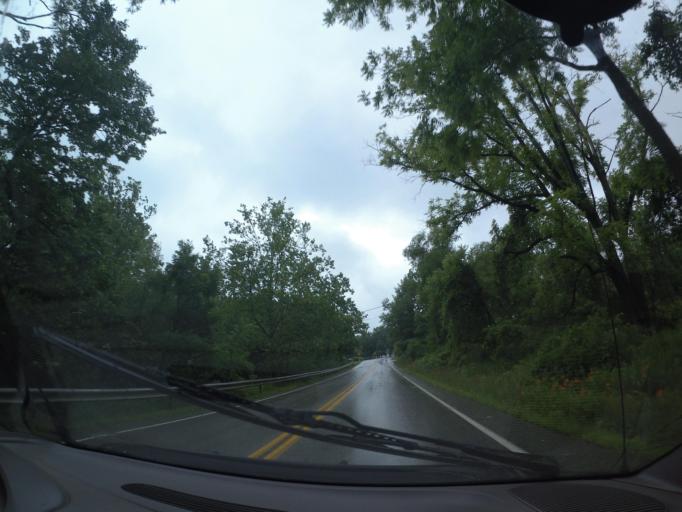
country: US
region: Pennsylvania
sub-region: Erie County
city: Fairview
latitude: 42.0021
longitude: -80.2060
